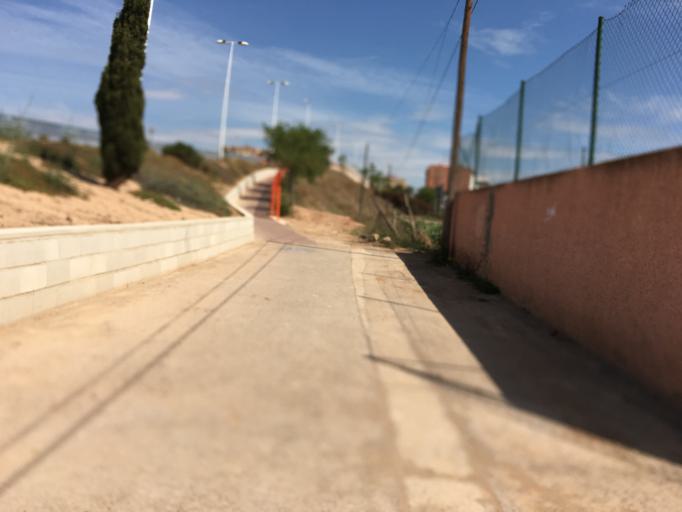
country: ES
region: Valencia
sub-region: Provincia de Valencia
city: Paterna
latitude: 39.4948
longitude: -0.4188
